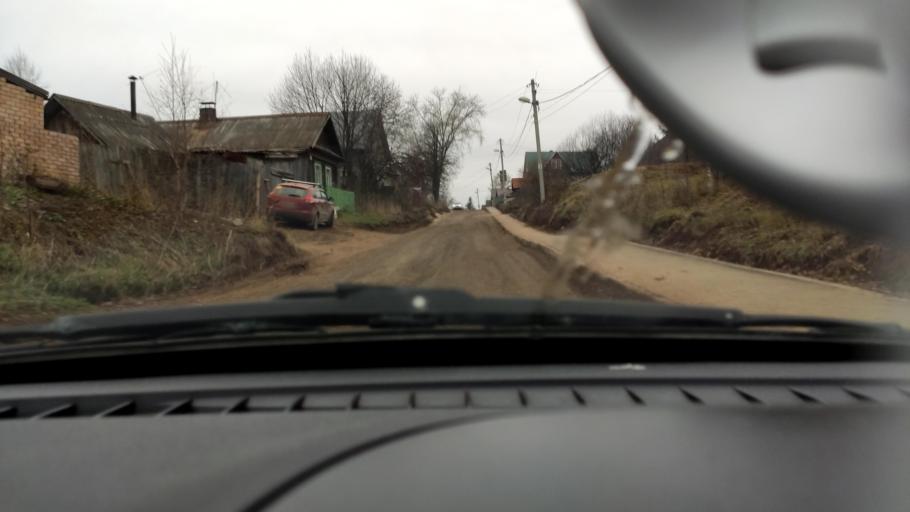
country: RU
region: Perm
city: Perm
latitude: 58.0278
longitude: 56.3398
